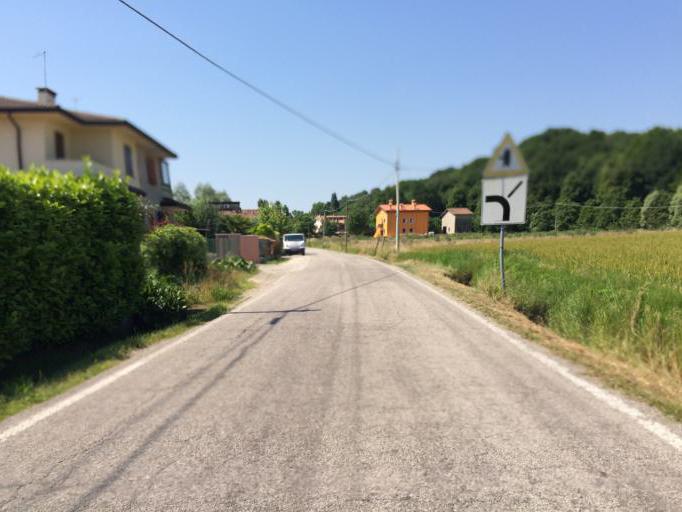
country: IT
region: Veneto
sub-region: Provincia di Vicenza
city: Montegalda
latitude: 45.4629
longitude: 11.6704
